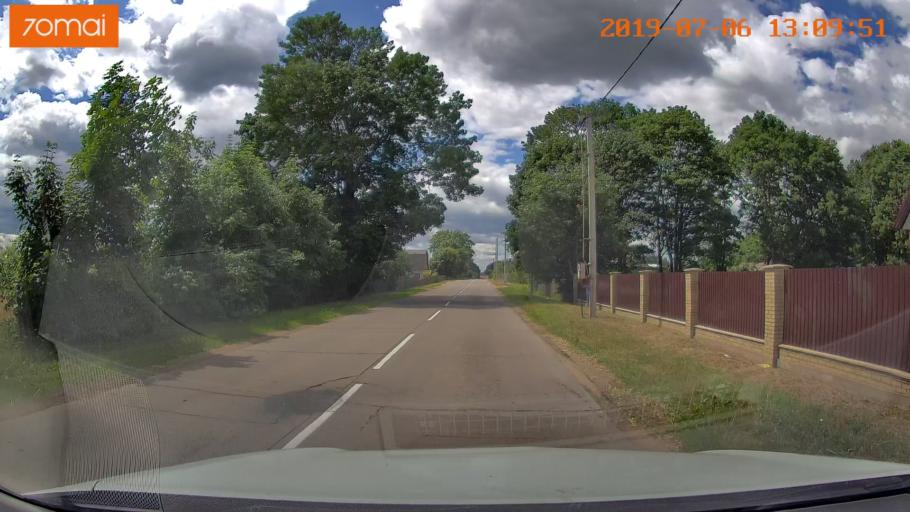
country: BY
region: Minsk
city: Enyerhyetykaw
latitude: 53.6604
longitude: 27.0090
